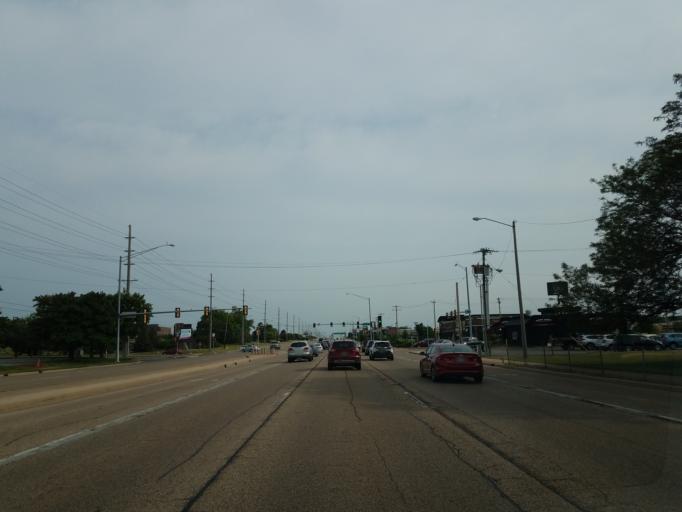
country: US
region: Illinois
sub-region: McLean County
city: Bloomington
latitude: 40.4791
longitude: -88.9525
